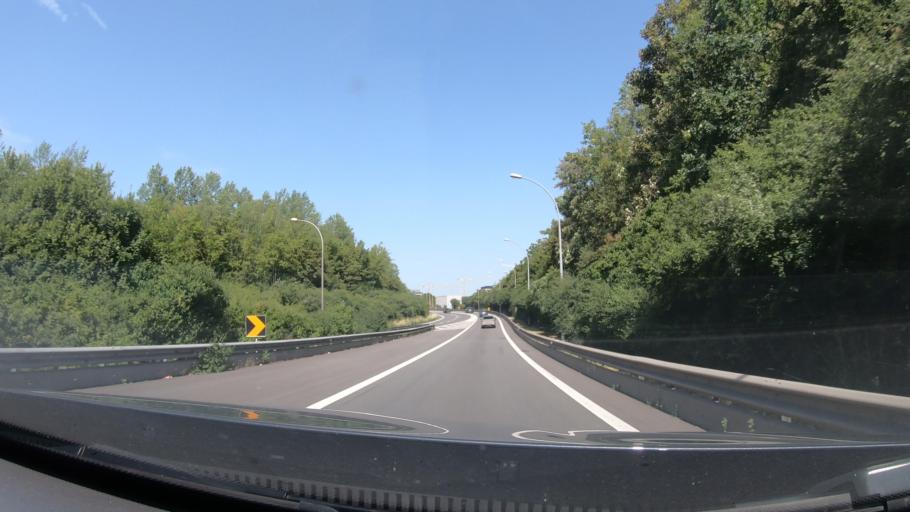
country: LU
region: Luxembourg
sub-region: Canton de Luxembourg
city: Hesperange
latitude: 49.5769
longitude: 6.1281
